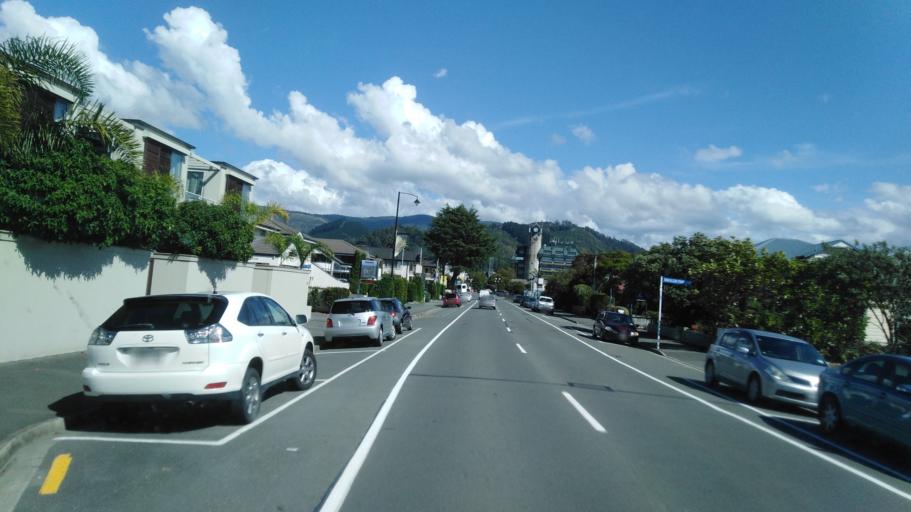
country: NZ
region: Nelson
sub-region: Nelson City
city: Nelson
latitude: -41.2677
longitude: 173.2841
